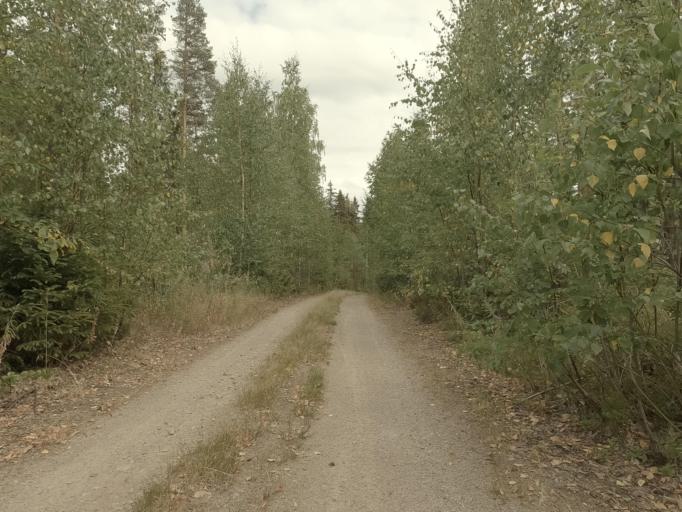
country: RU
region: Leningrad
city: Kamennogorsk
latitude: 61.0160
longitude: 29.2051
